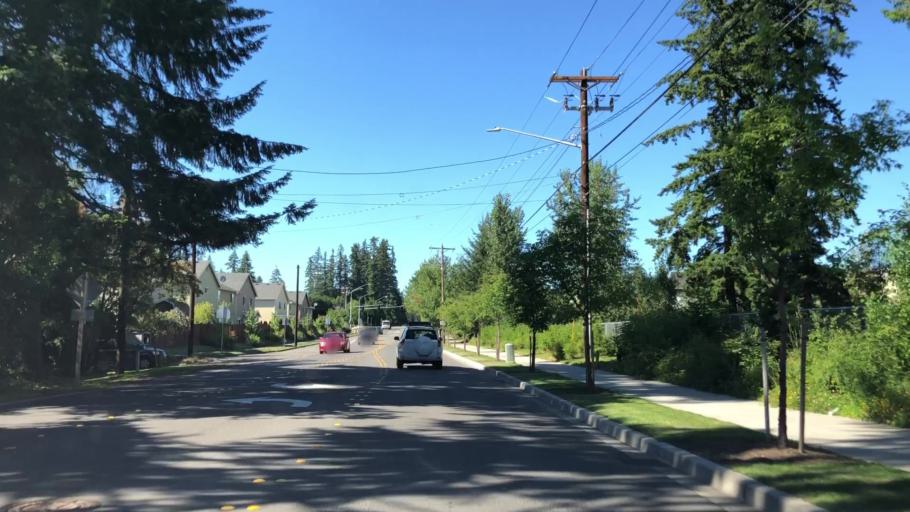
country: US
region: Washington
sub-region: Snohomish County
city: North Creek
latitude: 47.8245
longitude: -122.1859
